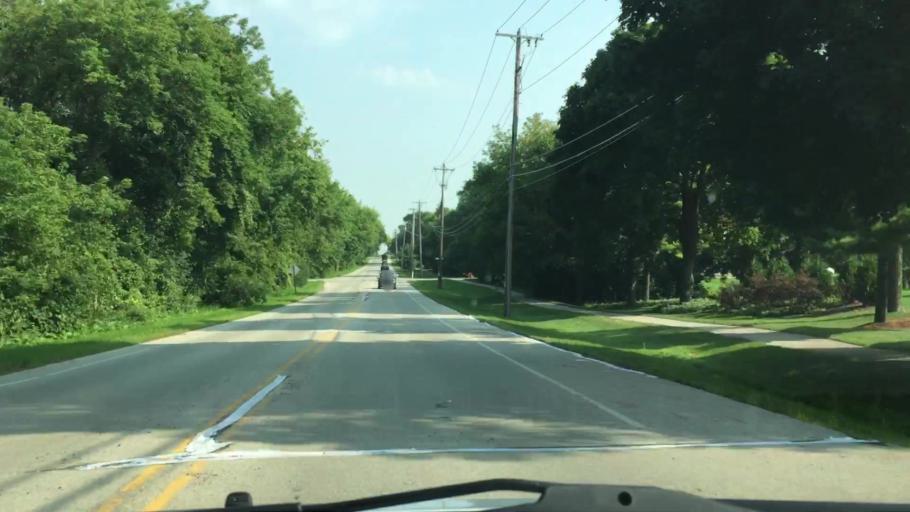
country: US
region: Wisconsin
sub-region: Waukesha County
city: Brookfield
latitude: 43.0548
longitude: -88.1462
